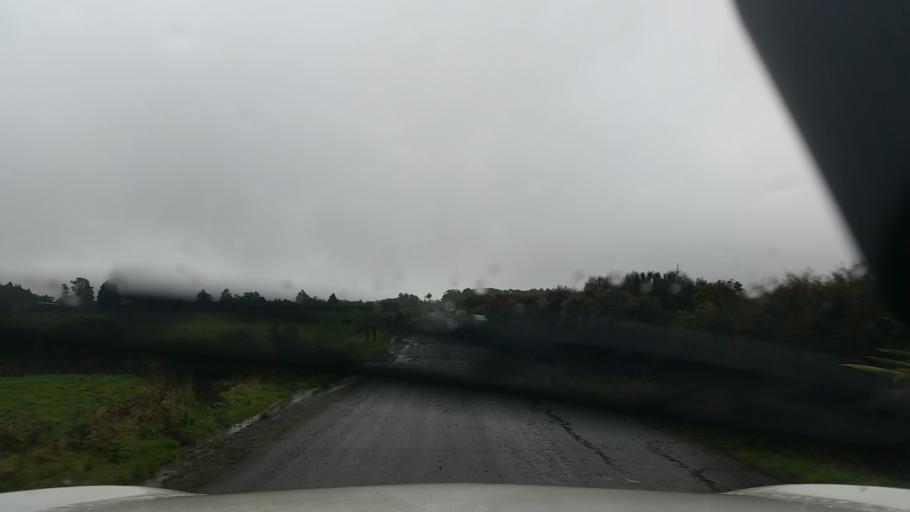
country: NZ
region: Taranaki
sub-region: South Taranaki District
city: Eltham
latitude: -39.2779
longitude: 174.1774
